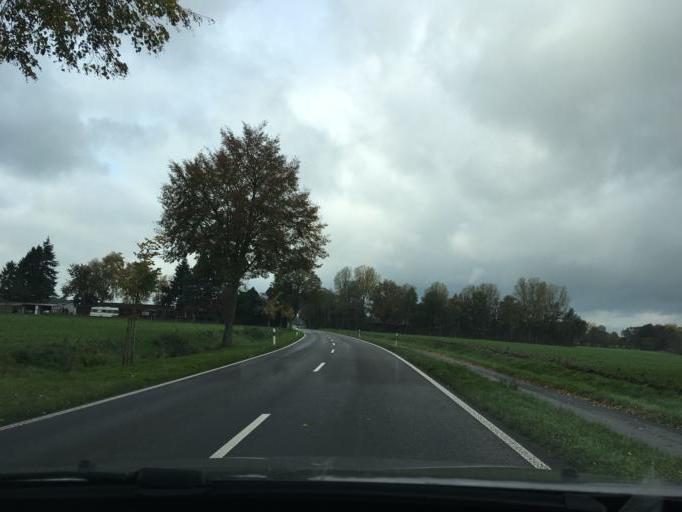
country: NL
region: Overijssel
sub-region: Gemeente Haaksbergen
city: Haaksbergen
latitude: 52.0920
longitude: 6.7717
